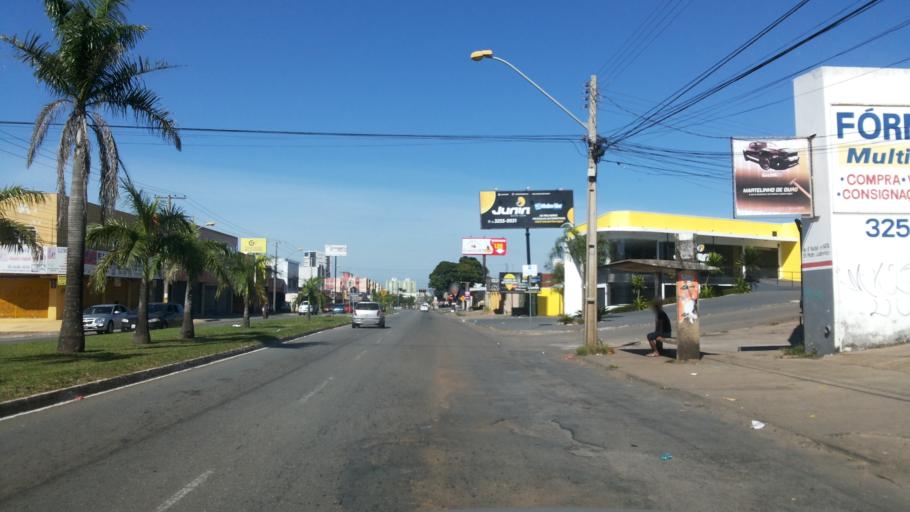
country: BR
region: Goias
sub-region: Goiania
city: Goiania
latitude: -16.7237
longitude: -49.2608
